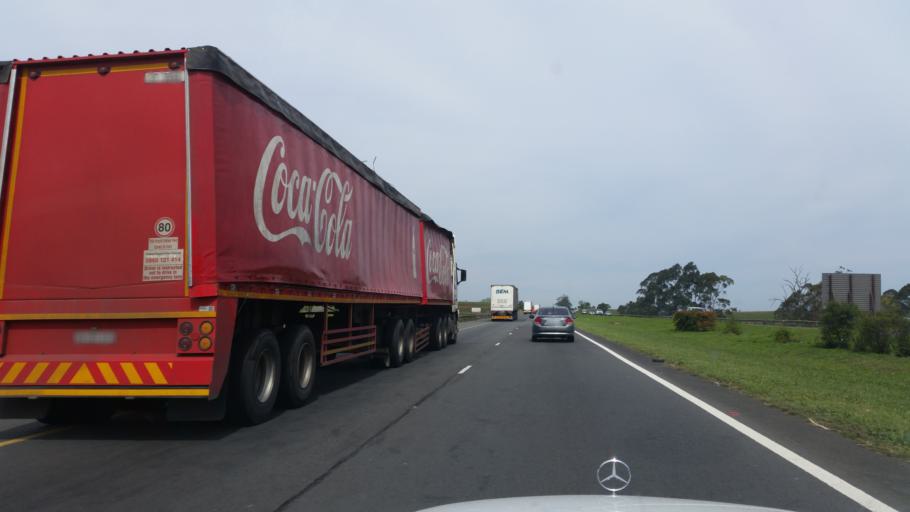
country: ZA
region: KwaZulu-Natal
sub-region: uMgungundlovu District Municipality
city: Camperdown
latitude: -29.7255
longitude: 30.5055
